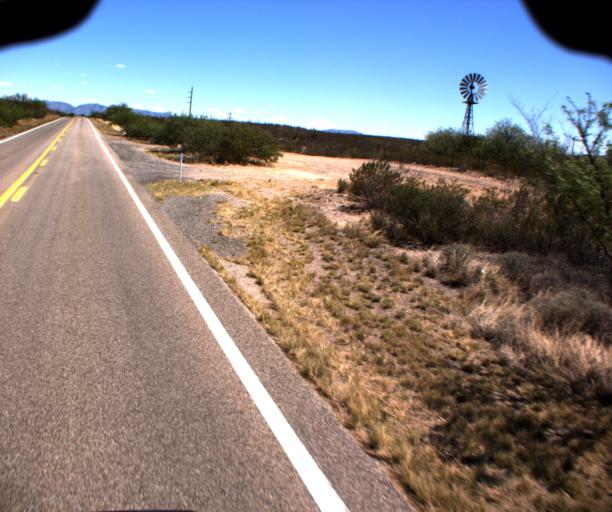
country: US
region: Arizona
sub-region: Cochise County
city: Tombstone
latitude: 31.7400
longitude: -110.1602
